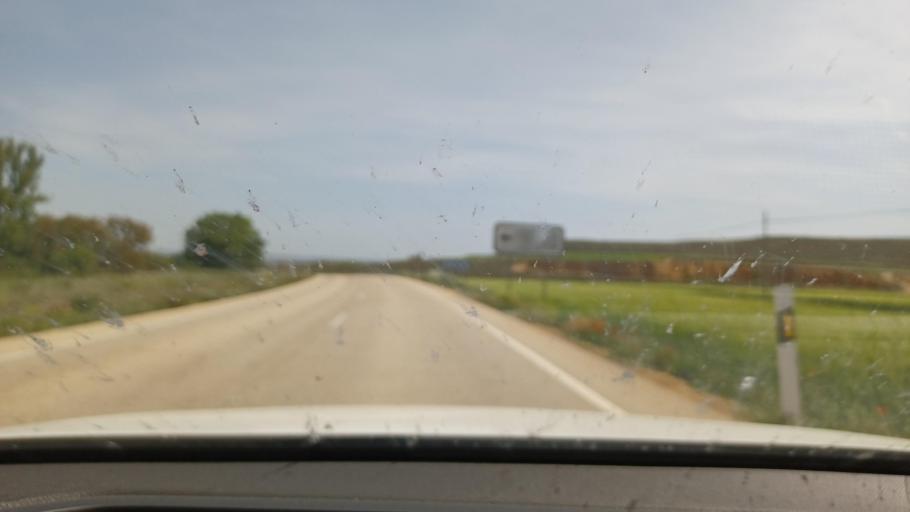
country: ES
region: Aragon
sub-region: Provincia de Zaragoza
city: Pozuel de Ariza
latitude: 41.3488
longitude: -2.1631
